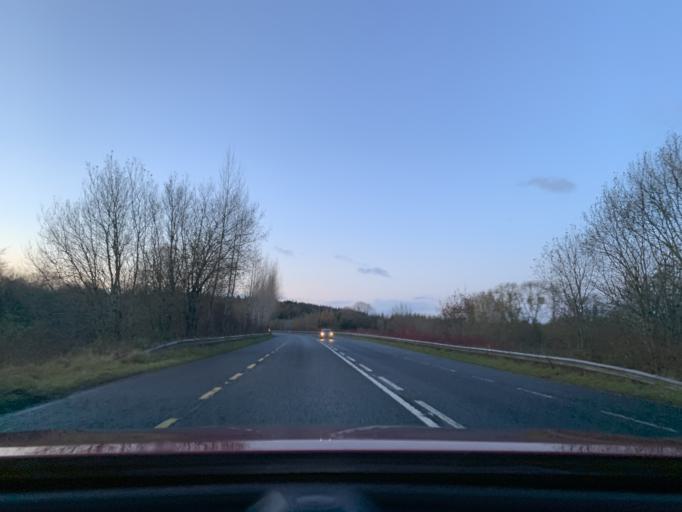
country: IE
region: Connaught
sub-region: County Leitrim
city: Carrick-on-Shannon
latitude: 53.9326
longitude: -8.0045
